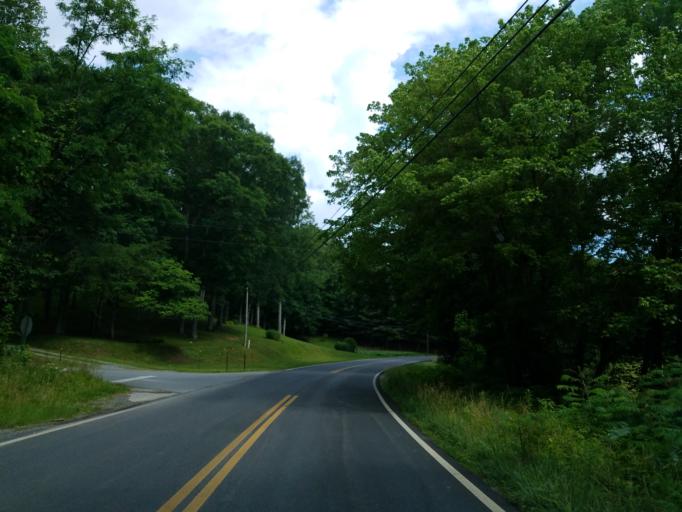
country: US
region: Georgia
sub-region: Fannin County
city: Blue Ridge
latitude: 34.8414
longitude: -84.2981
